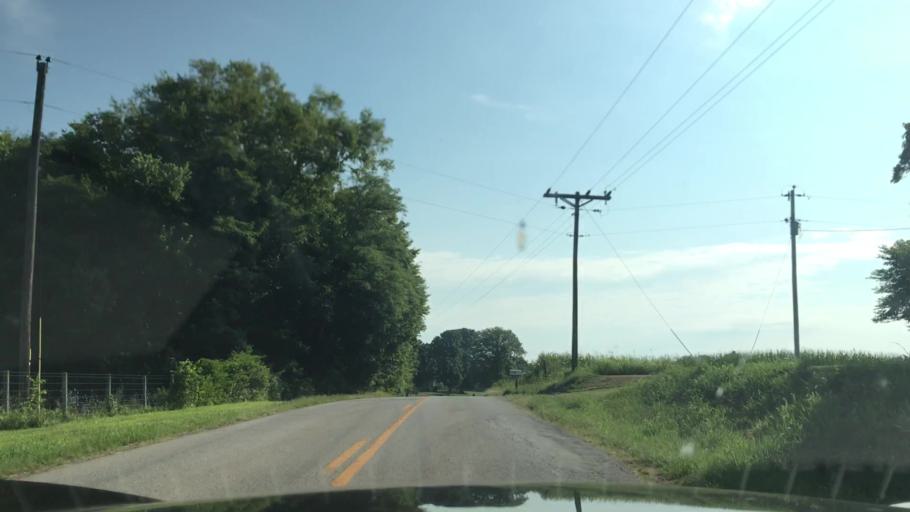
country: US
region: Kentucky
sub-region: Hart County
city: Horse Cave
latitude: 37.1857
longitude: -85.7710
